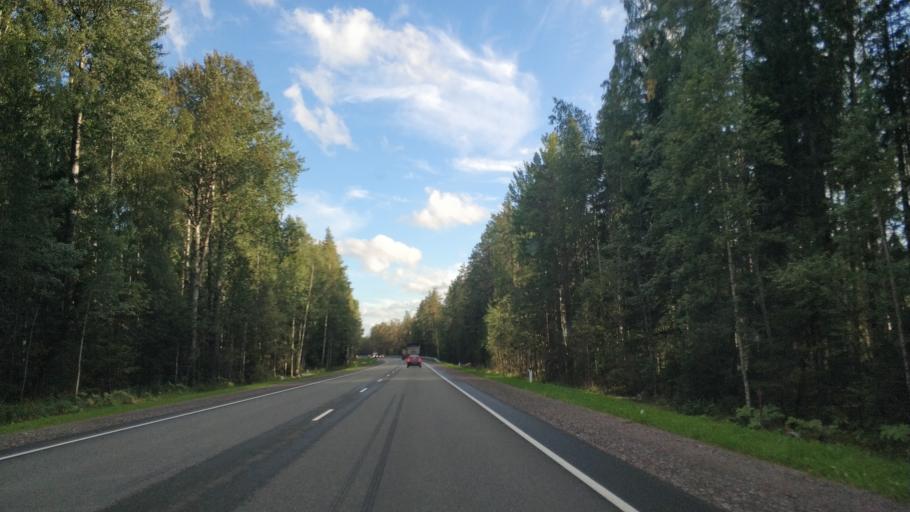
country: RU
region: Leningrad
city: Priozersk
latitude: 60.8938
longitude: 30.1596
